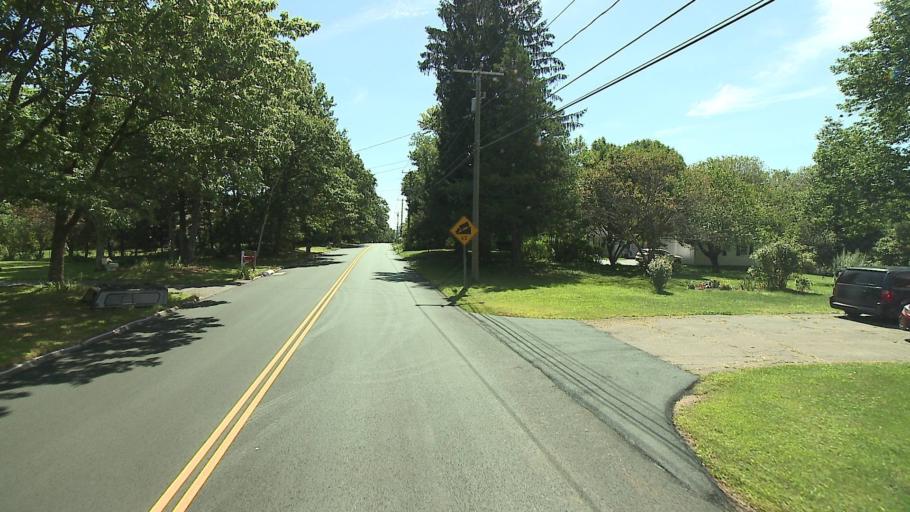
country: US
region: Connecticut
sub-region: Hartford County
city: West Simsbury
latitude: 41.9269
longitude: -72.9118
